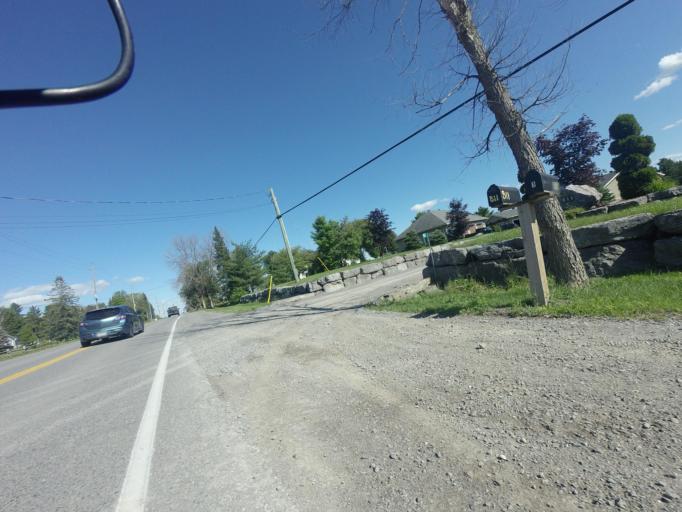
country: CA
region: Ontario
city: Arnprior
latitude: 45.4171
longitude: -76.4246
